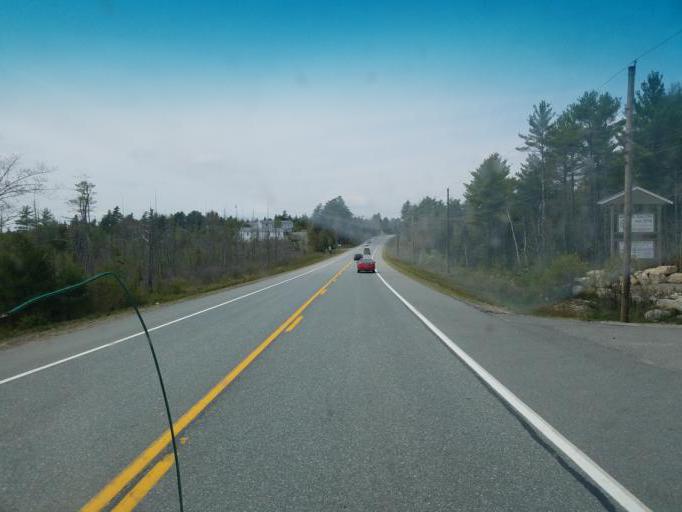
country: US
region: Maine
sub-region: Hancock County
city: Ellsworth
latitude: 44.5825
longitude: -68.4847
